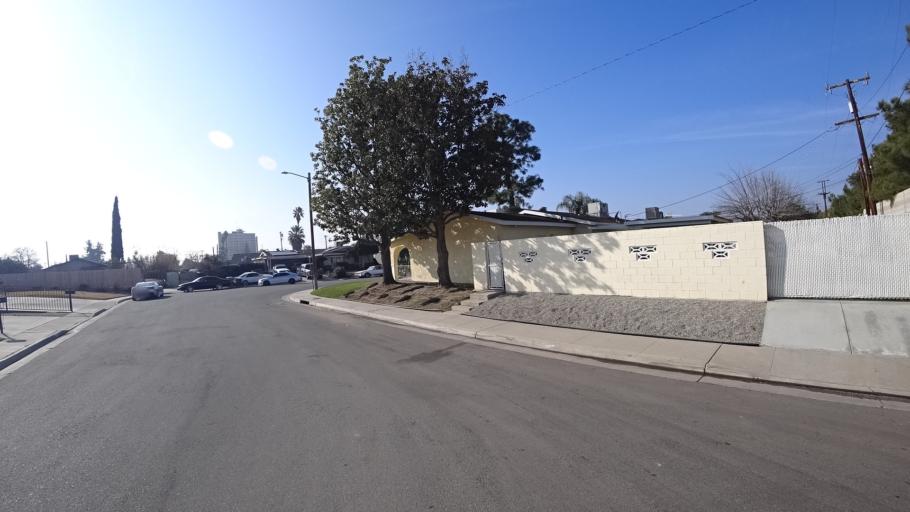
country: US
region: California
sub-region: Kern County
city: Bakersfield
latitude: 35.3349
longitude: -119.0354
